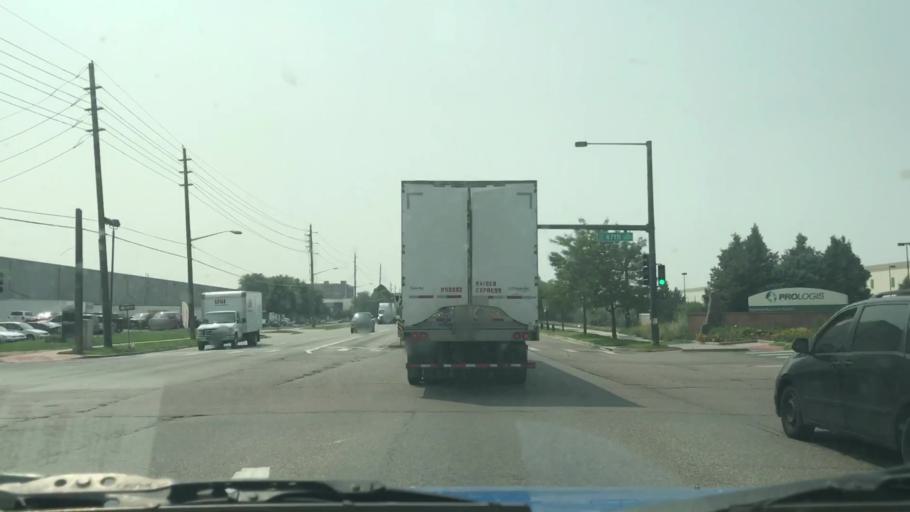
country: US
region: Colorado
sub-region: Adams County
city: Aurora
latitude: 39.7832
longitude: -104.8659
